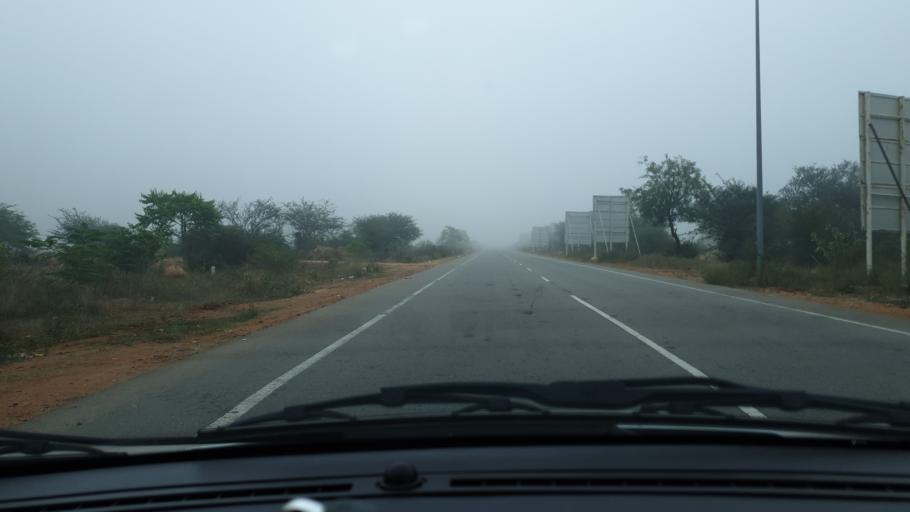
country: IN
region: Telangana
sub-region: Nalgonda
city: Devarkonda
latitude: 16.6107
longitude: 78.6765
